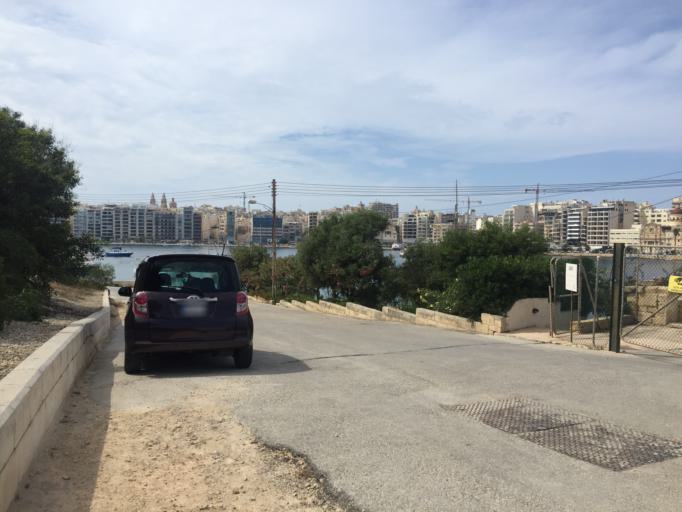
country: MT
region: Tas-Sliema
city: Sliema
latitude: 35.9046
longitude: 14.5060
